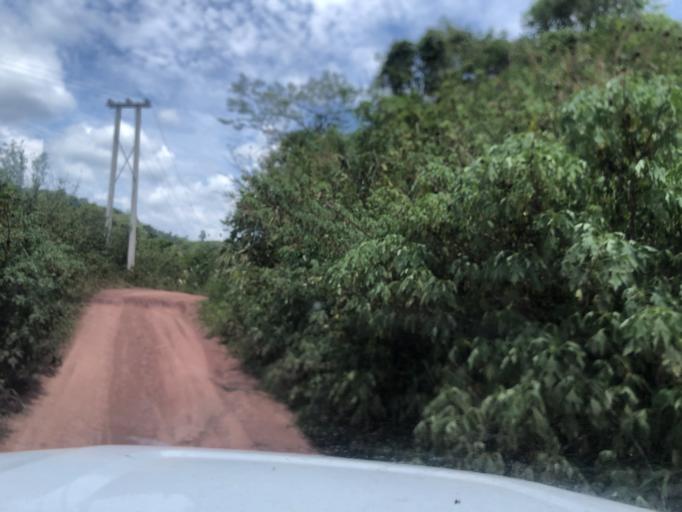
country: CN
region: Yunnan
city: Menglie
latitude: 22.2417
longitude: 101.6125
